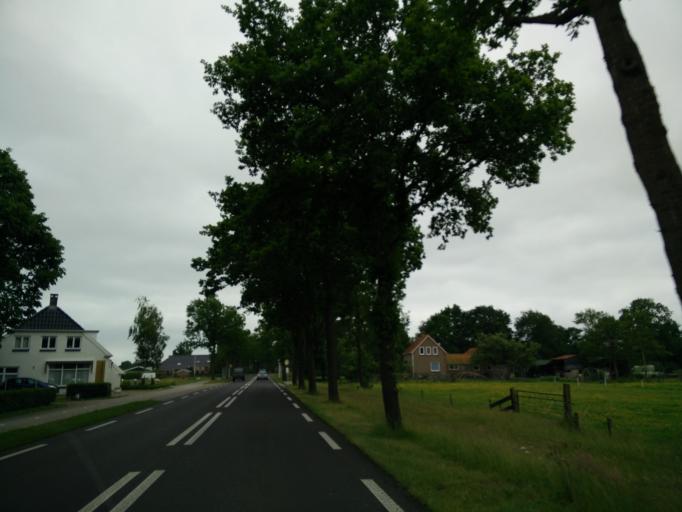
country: NL
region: Groningen
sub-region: Gemeente Groningen
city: Groningen
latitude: 53.1637
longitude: 6.4962
